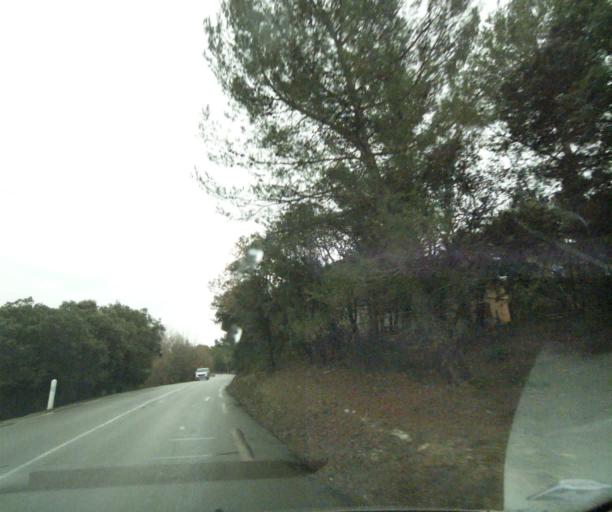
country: FR
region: Provence-Alpes-Cote d'Azur
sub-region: Departement des Bouches-du-Rhone
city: Lambesc
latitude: 43.6567
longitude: 5.2867
